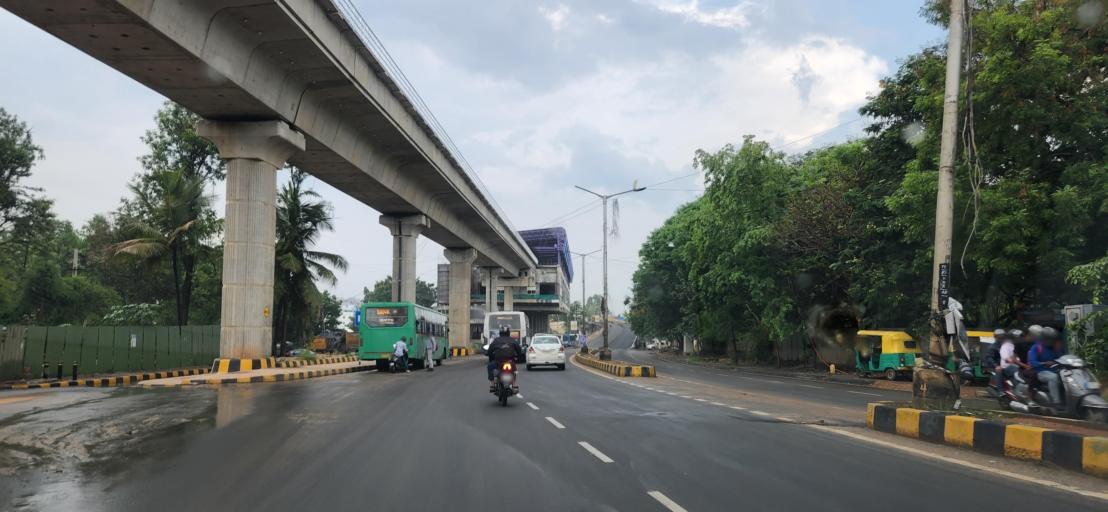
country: IN
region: Karnataka
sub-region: Bangalore Rural
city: Hoskote
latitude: 12.9925
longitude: 77.7573
